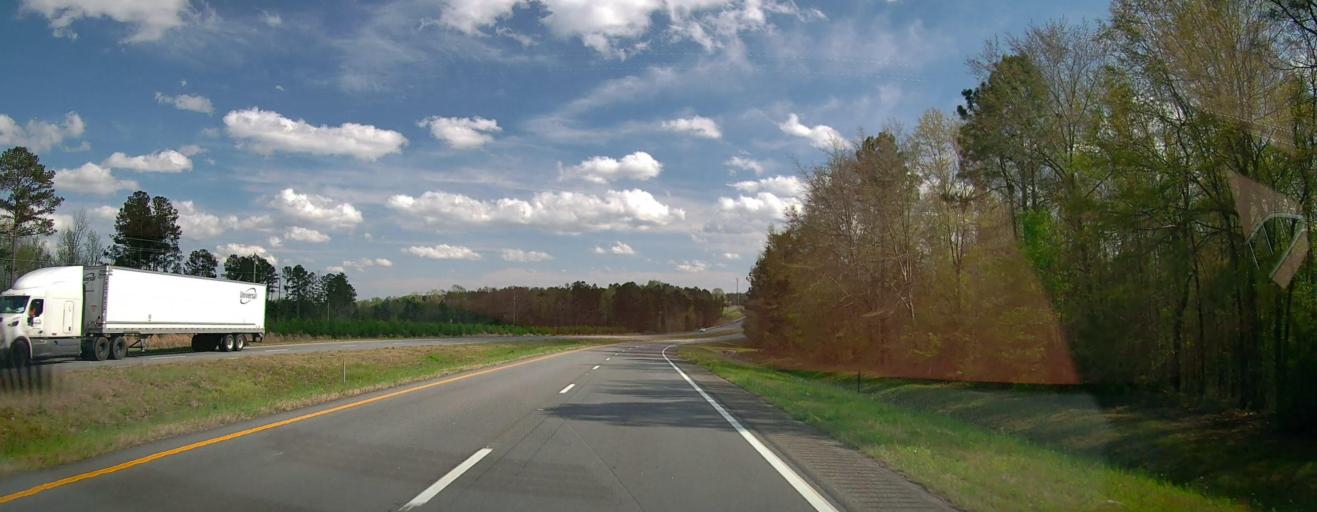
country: US
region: Georgia
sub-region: Baldwin County
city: Hardwick
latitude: 33.0092
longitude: -83.2230
